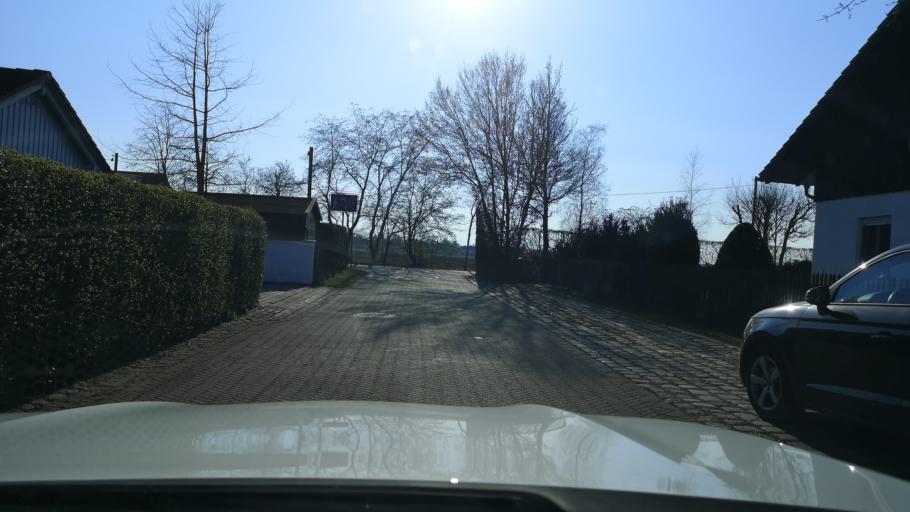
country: DE
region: Bavaria
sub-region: Upper Bavaria
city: Kirchheim bei Muenchen
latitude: 48.1807
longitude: 11.7564
